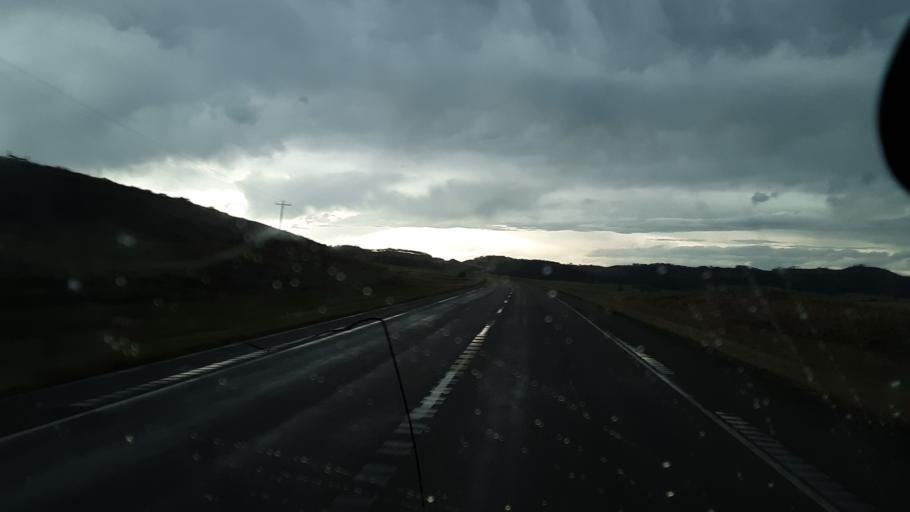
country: US
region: Montana
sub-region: Powder River County
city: Broadus
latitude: 45.5452
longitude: -105.8430
